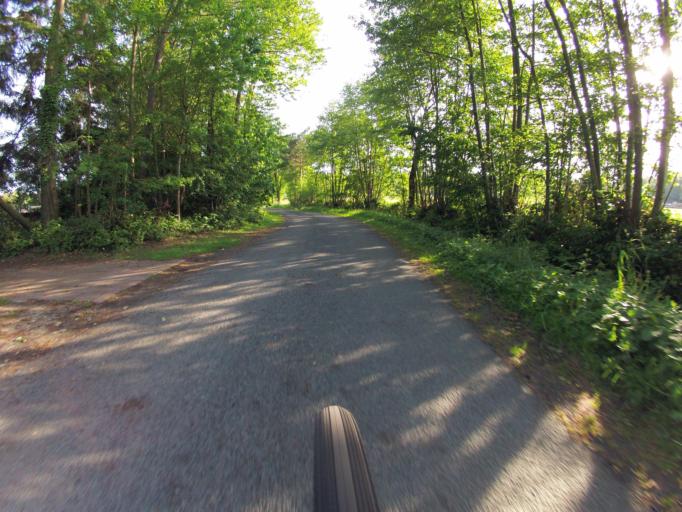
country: DE
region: North Rhine-Westphalia
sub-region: Regierungsbezirk Munster
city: Birgte
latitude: 52.2695
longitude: 7.6701
